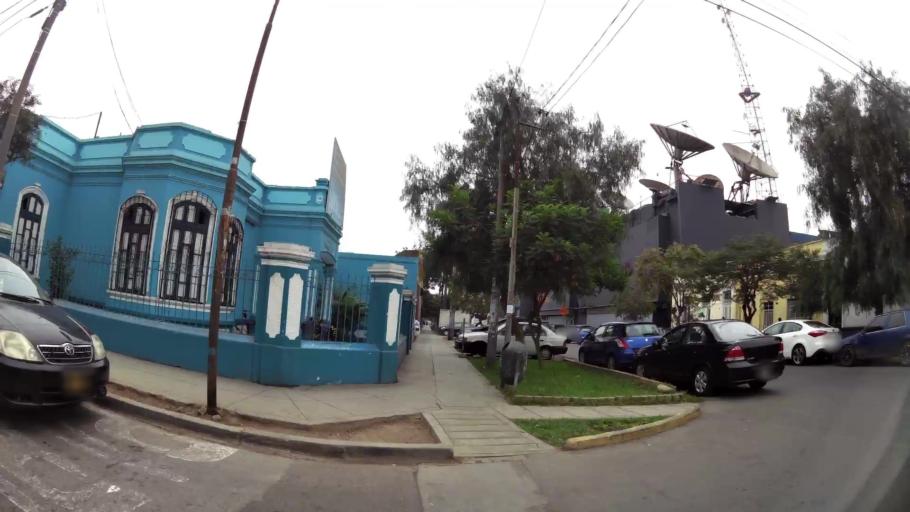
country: PE
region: Lima
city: Lima
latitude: -12.0753
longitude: -77.0331
